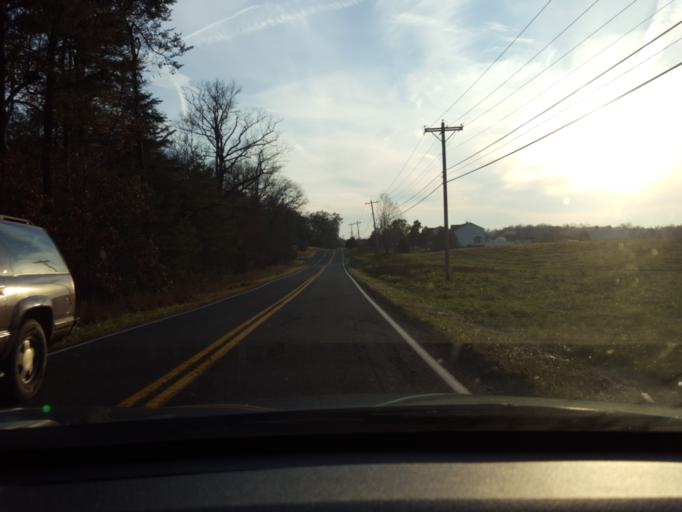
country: US
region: Maryland
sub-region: Saint Mary's County
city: Charlotte Hall
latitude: 38.4957
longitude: -76.8696
